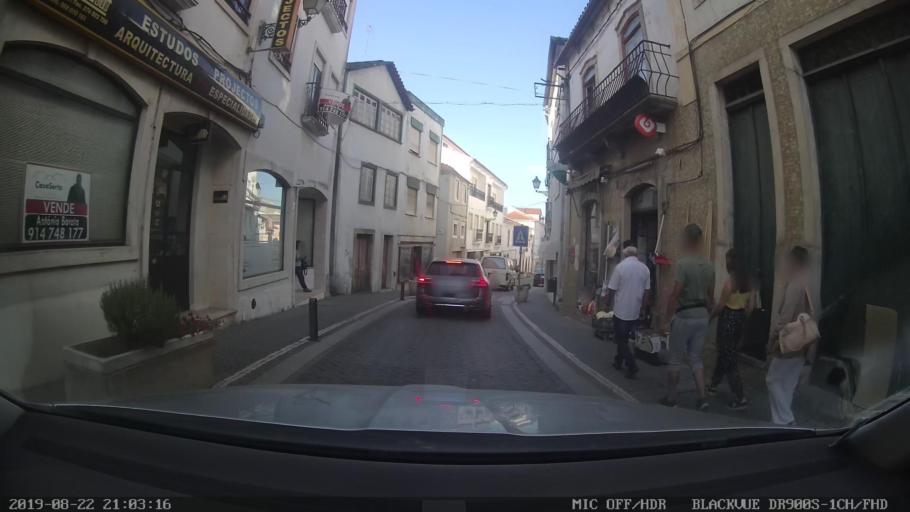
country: PT
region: Castelo Branco
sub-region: Serta
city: Serta
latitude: 39.8066
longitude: -8.0983
